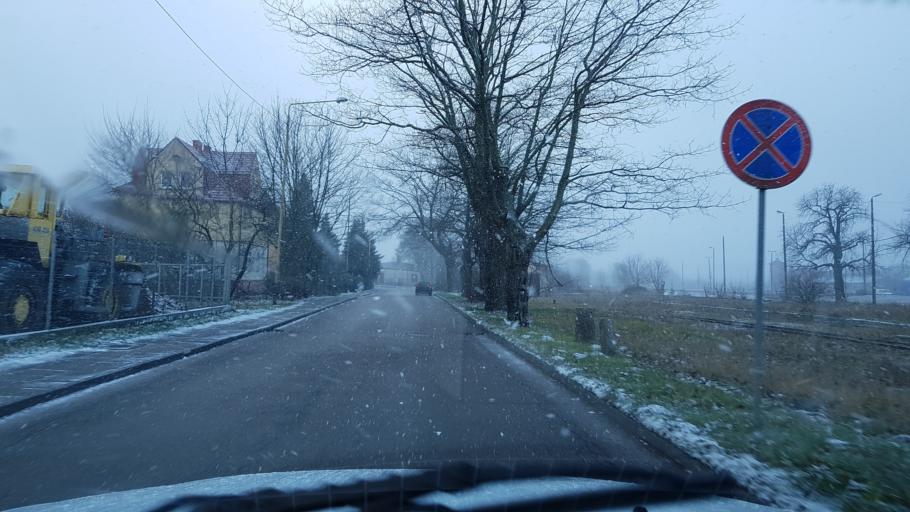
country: PL
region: West Pomeranian Voivodeship
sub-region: Powiat gryficki
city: Trzebiatow
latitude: 54.0608
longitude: 15.2793
